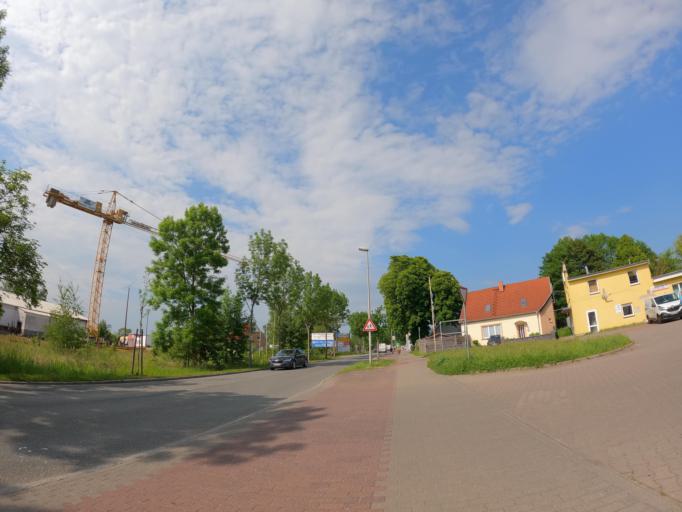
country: DE
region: Mecklenburg-Vorpommern
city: Stralsund
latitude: 54.3016
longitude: 13.0625
